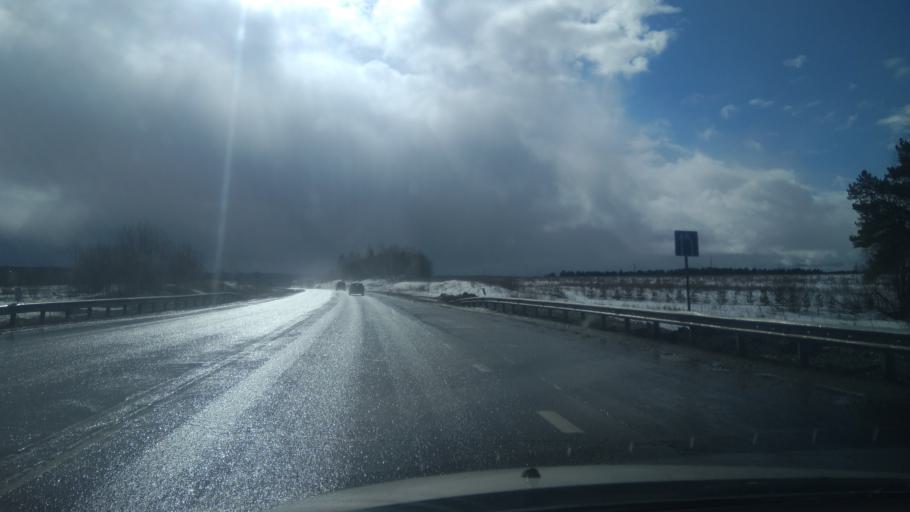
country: RU
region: Perm
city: Kungur
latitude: 57.3812
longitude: 56.9060
